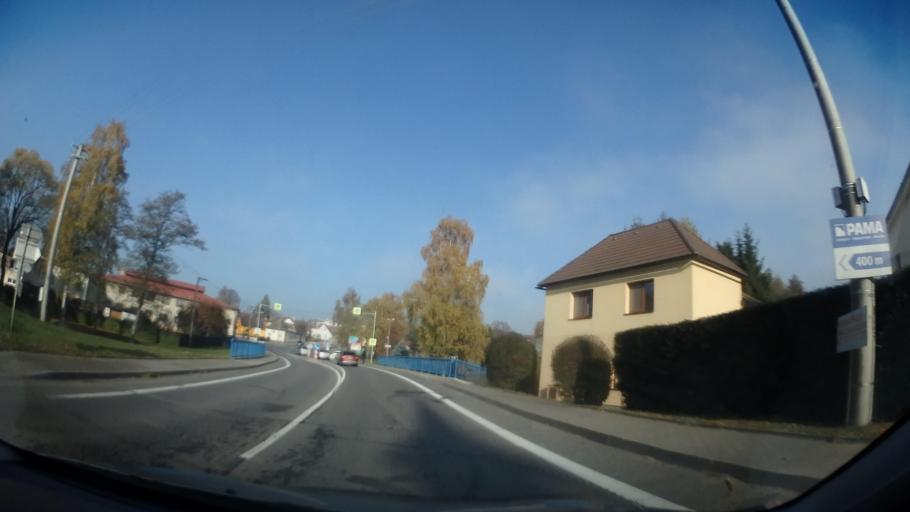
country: CZ
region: Vysocina
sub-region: Okres Zd'ar nad Sazavou
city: Nove Veseli
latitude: 49.4881
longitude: 15.9896
